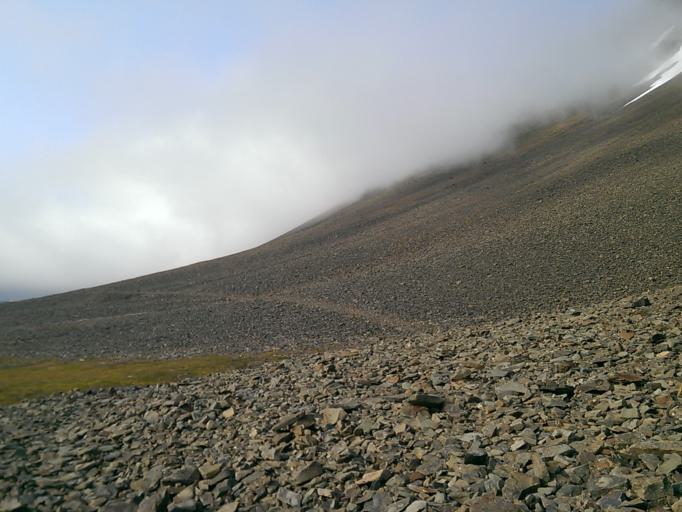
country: SJ
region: Svalbard
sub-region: Spitsbergen
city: Longyearbyen
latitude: 78.2195
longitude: 15.3391
